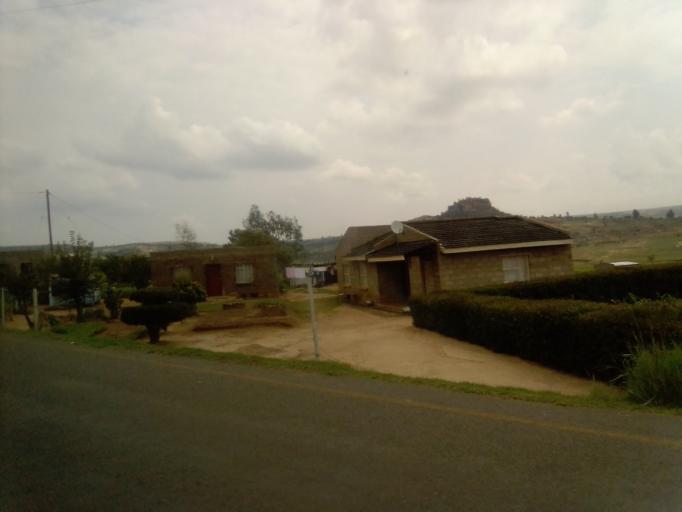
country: LS
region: Leribe
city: Leribe
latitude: -29.0151
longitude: 28.0014
